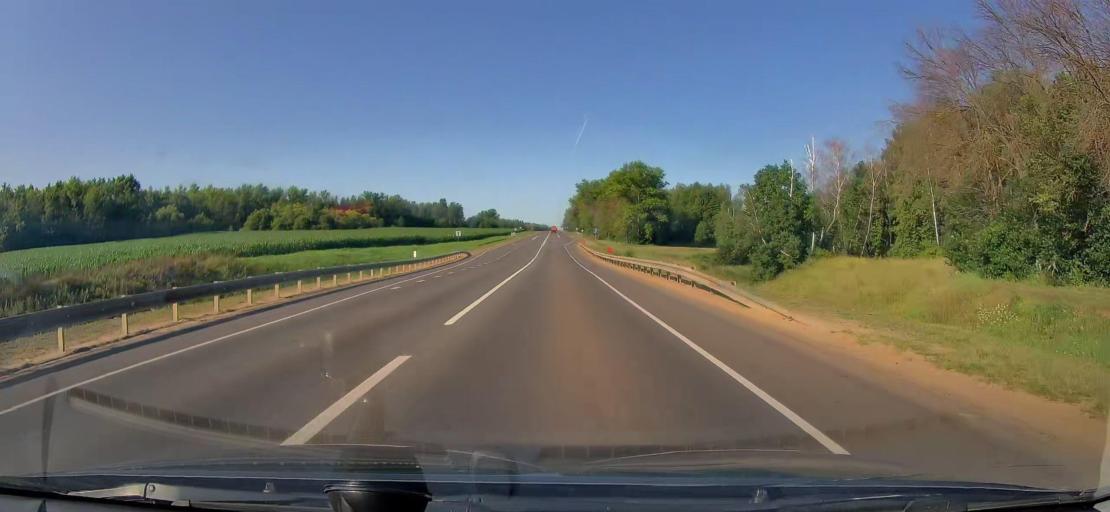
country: RU
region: Orjol
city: Mtsensk
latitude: 53.1312
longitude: 36.3354
